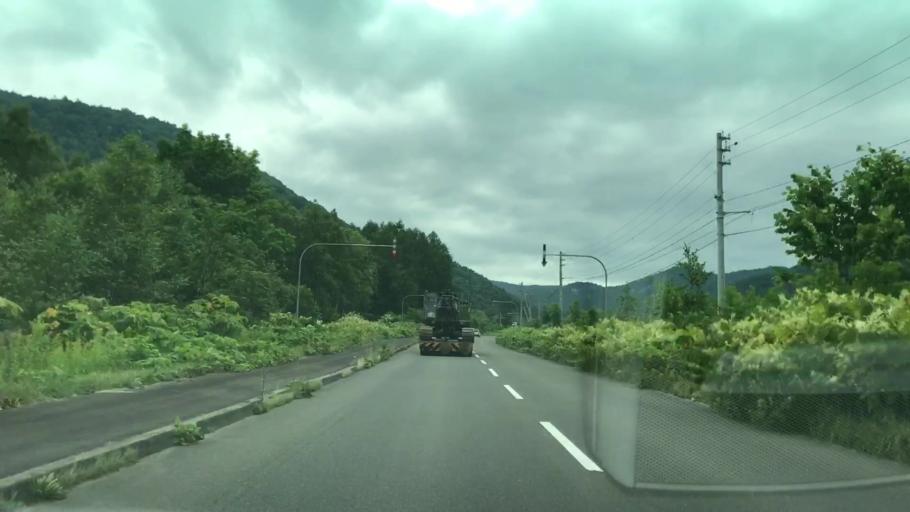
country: JP
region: Hokkaido
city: Yoichi
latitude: 43.0315
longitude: 140.8652
